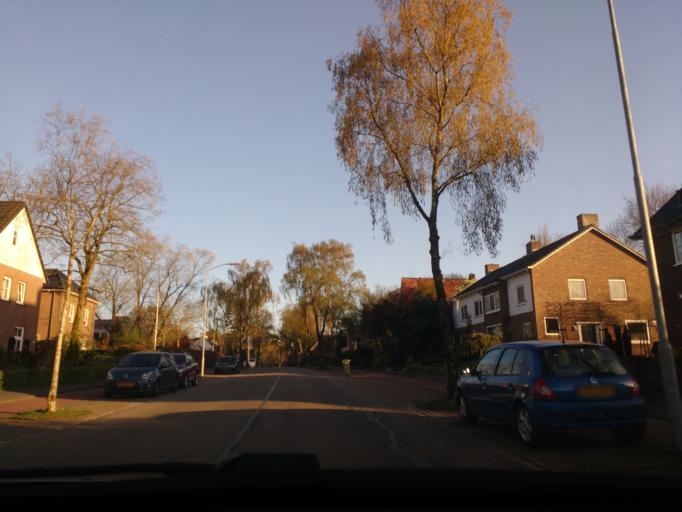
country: NL
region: Gelderland
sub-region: Gemeente Wageningen
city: Wageningen
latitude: 51.9696
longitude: 5.6834
